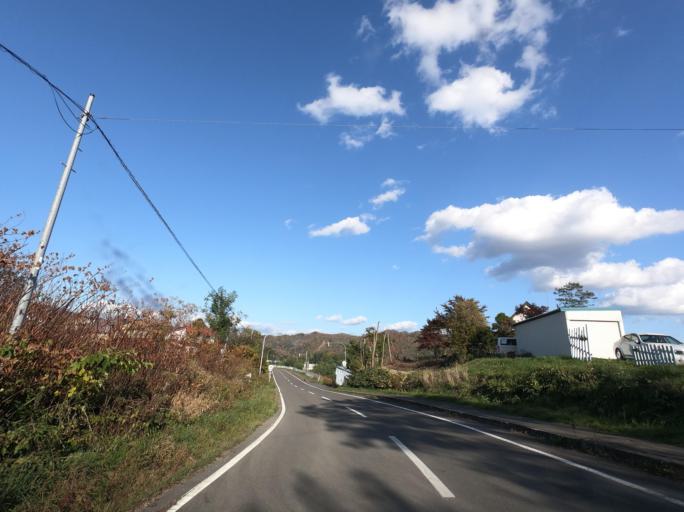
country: JP
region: Hokkaido
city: Iwamizawa
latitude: 42.9837
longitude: 142.0015
